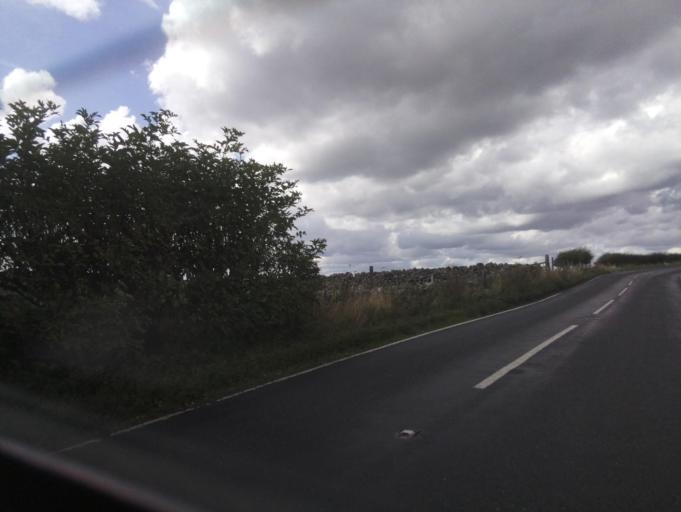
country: GB
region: England
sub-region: North Yorkshire
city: Leyburn
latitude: 54.3668
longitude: -1.8253
